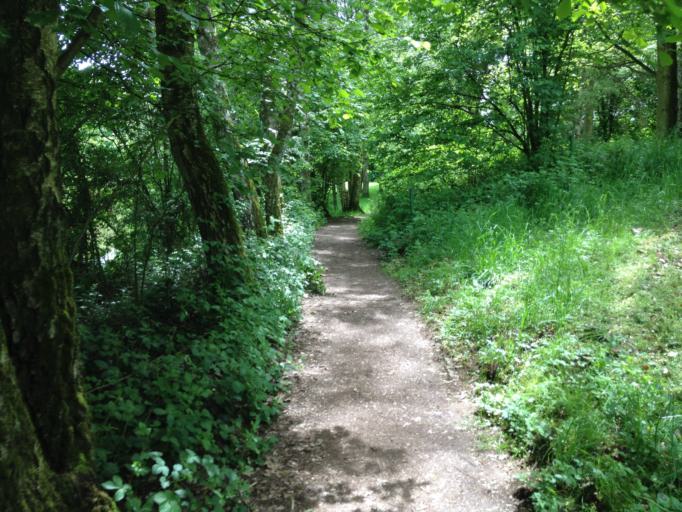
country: DE
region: Saarland
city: Ottweiler
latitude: 49.3866
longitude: 7.1791
